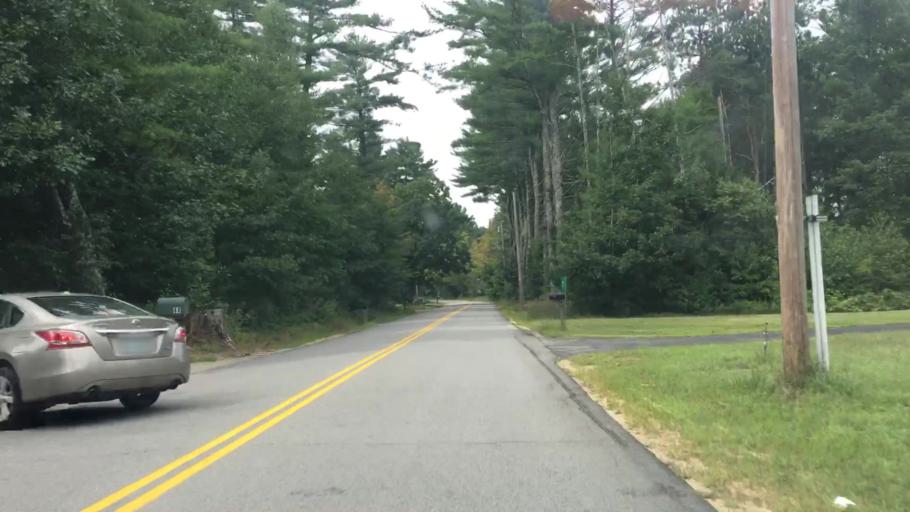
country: US
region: New Hampshire
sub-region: Strafford County
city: Barrington
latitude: 43.1993
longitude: -70.9938
